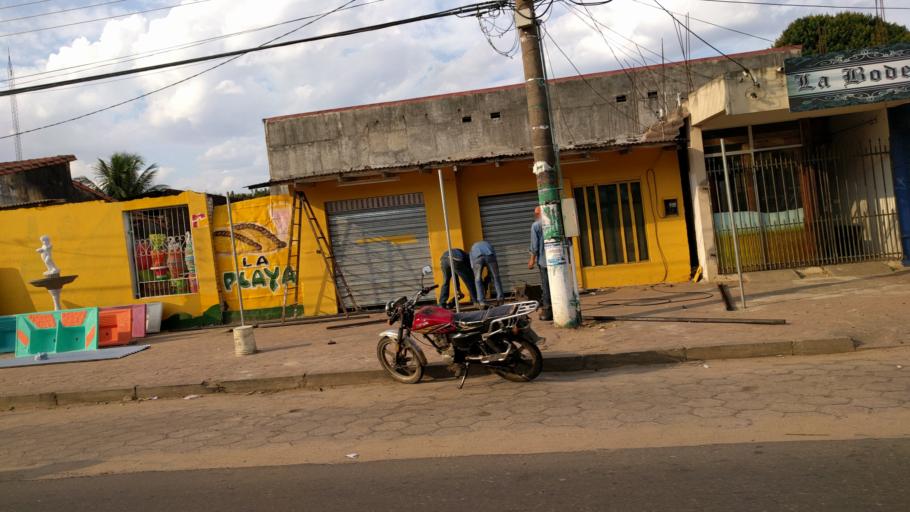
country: BO
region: Santa Cruz
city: Warnes
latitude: -17.5137
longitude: -63.1661
